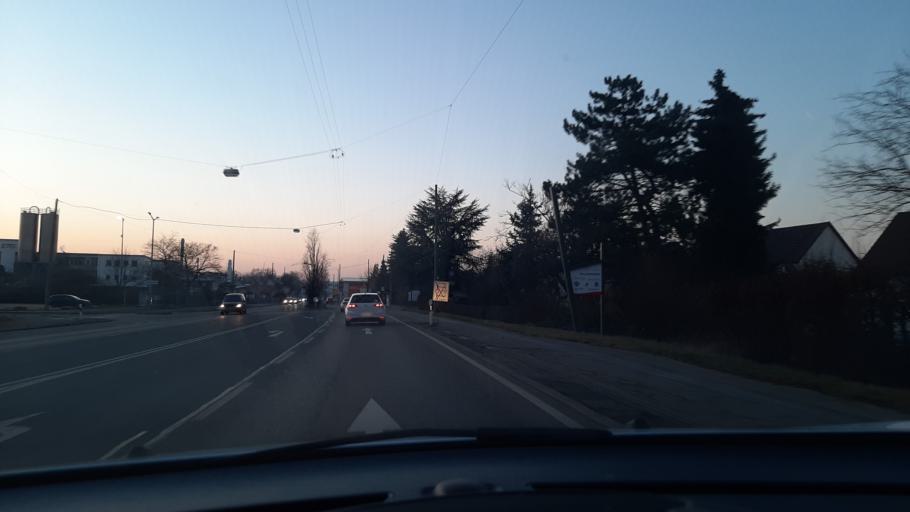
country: DE
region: Baden-Wuerttemberg
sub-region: Regierungsbezirk Stuttgart
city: Eislingen
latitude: 48.6905
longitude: 9.7215
